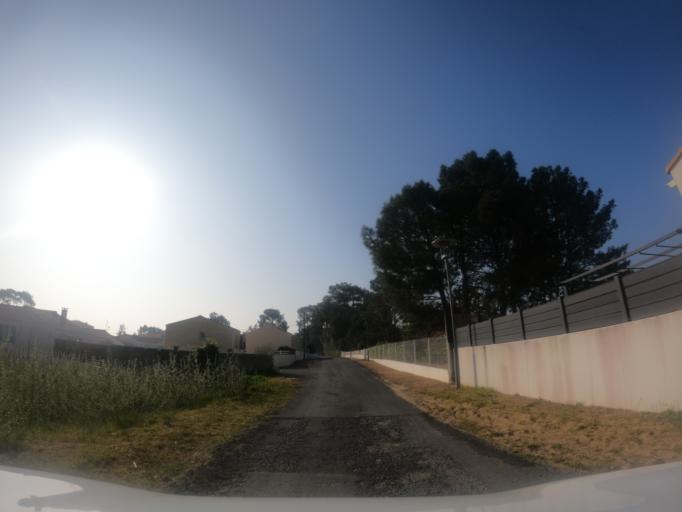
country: FR
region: Pays de la Loire
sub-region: Departement de la Vendee
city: La Tranche-sur-Mer
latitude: 46.3490
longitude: -1.4469
